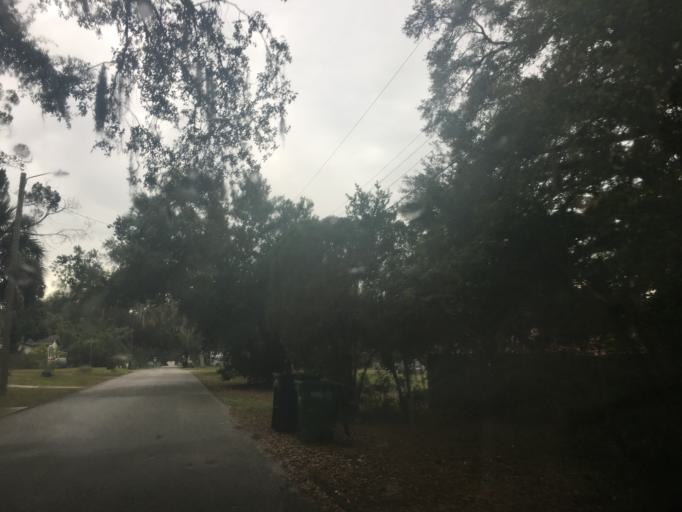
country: US
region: Florida
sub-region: Hillsborough County
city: Tampa
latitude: 27.9797
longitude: -82.4628
